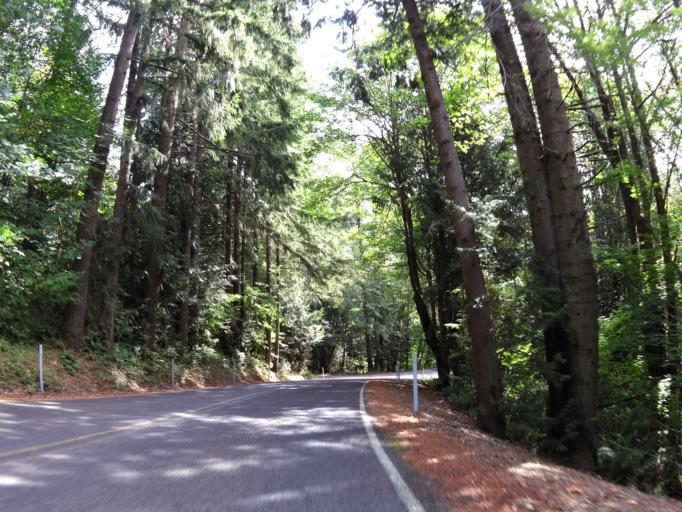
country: US
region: Washington
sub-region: Lewis County
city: Napavine
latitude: 46.5918
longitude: -122.9722
